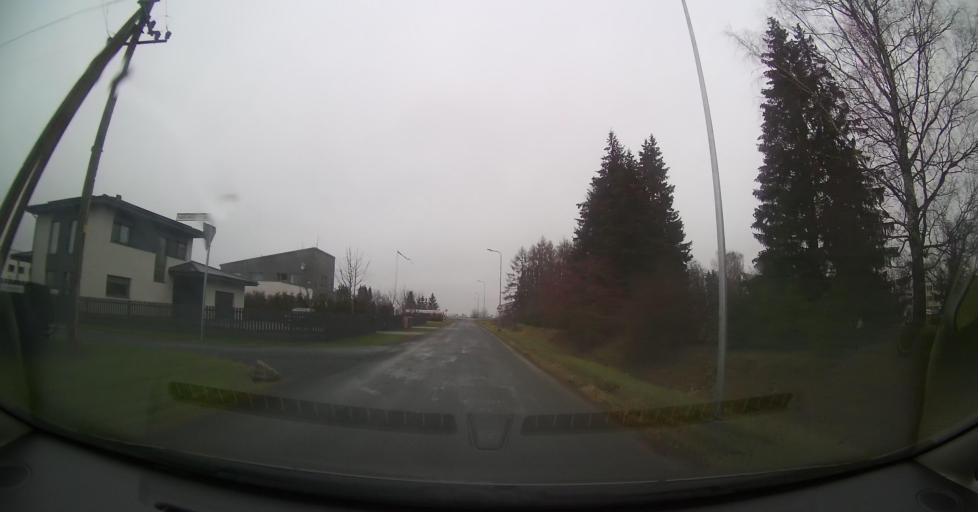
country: EE
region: Tartu
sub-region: Tartu linn
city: Tartu
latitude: 58.3544
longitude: 26.8711
